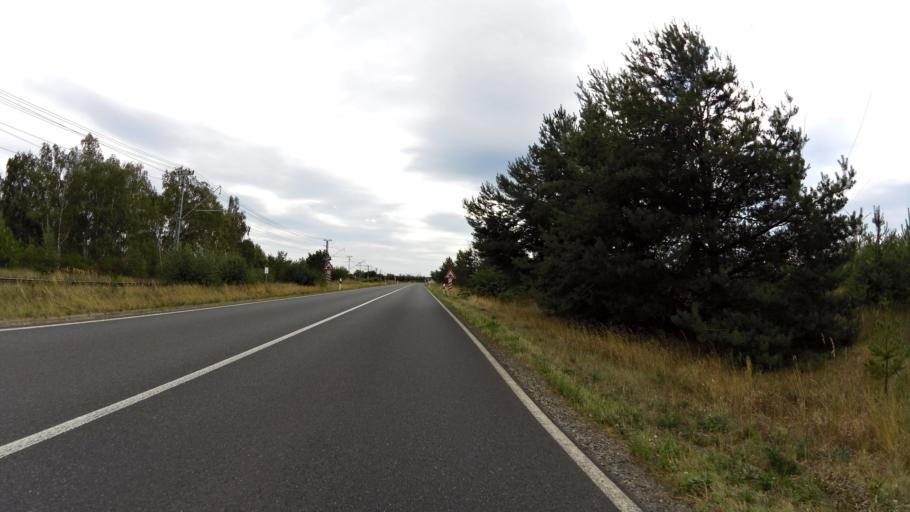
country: DE
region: Brandenburg
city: Heinersbruck
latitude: 51.7948
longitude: 14.4844
